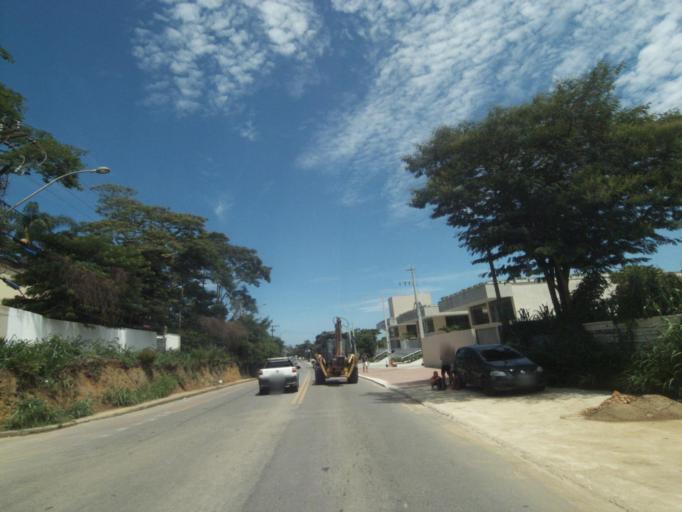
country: BR
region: Rio de Janeiro
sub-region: Niteroi
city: Niteroi
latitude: -22.9400
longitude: -43.0162
